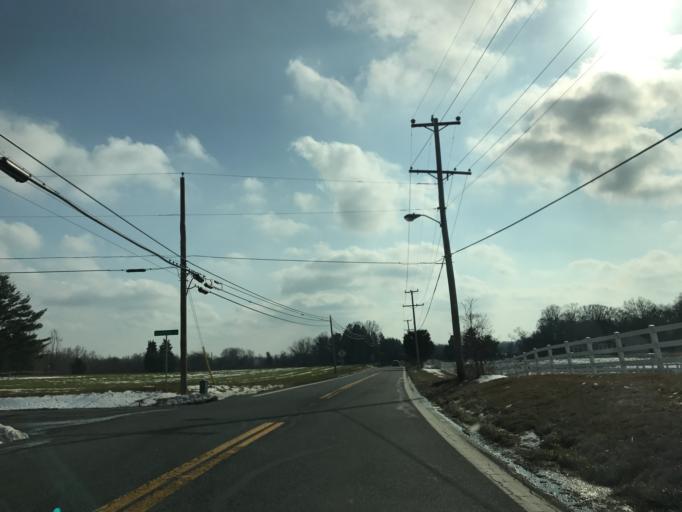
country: US
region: Maryland
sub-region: Harford County
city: Riverside
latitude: 39.5459
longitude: -76.2528
